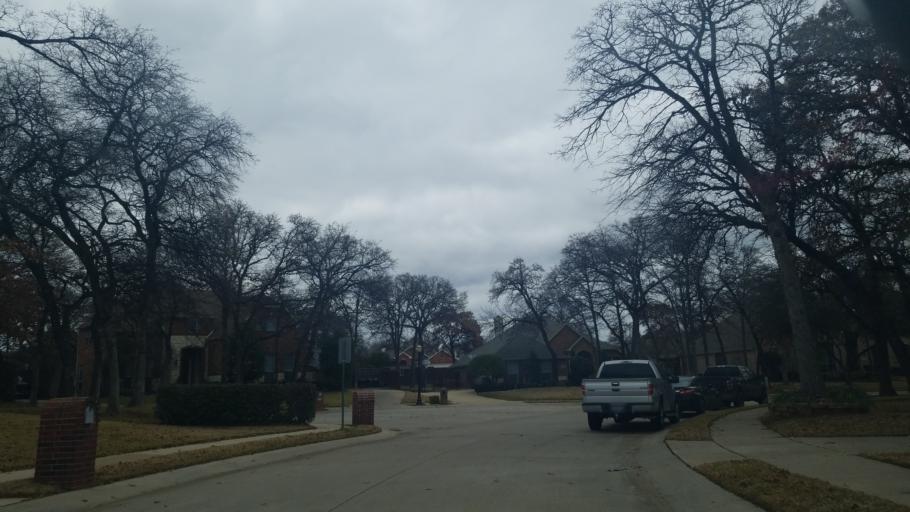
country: US
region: Texas
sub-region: Denton County
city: Corinth
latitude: 33.1350
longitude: -97.0836
